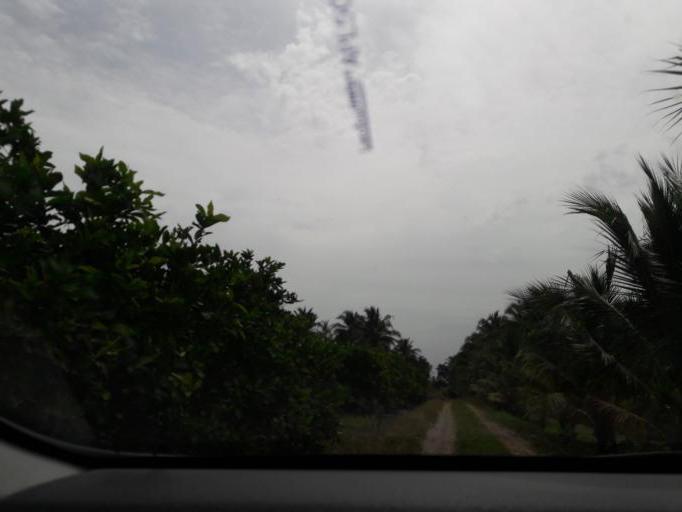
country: TH
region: Ratchaburi
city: Damnoen Saduak
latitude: 13.5622
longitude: 99.9954
